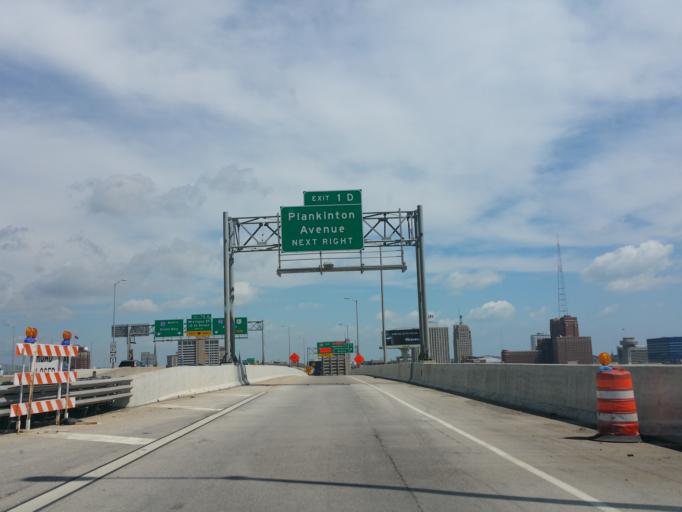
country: US
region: Wisconsin
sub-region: Milwaukee County
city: Milwaukee
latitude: 43.0301
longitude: -87.9224
